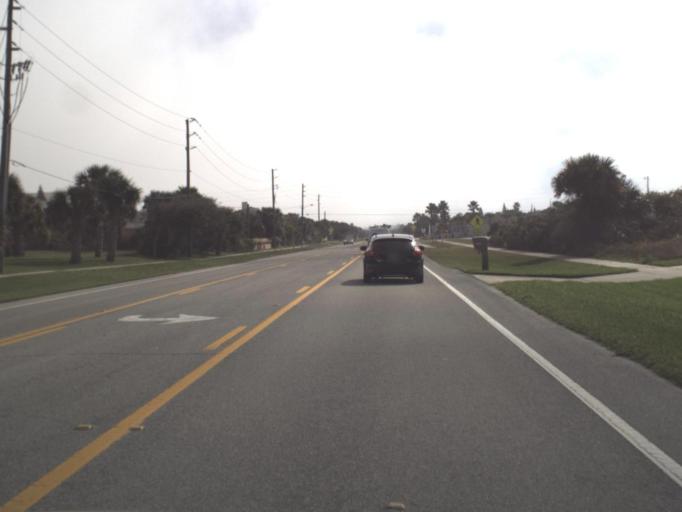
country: US
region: Florida
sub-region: Volusia County
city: Edgewater
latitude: 28.9918
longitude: -80.8686
